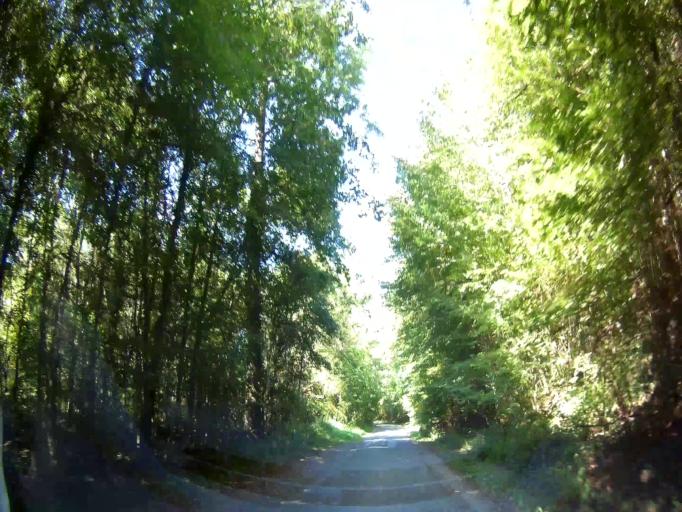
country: BE
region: Wallonia
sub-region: Province de Namur
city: Houyet
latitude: 50.2267
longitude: 4.9810
